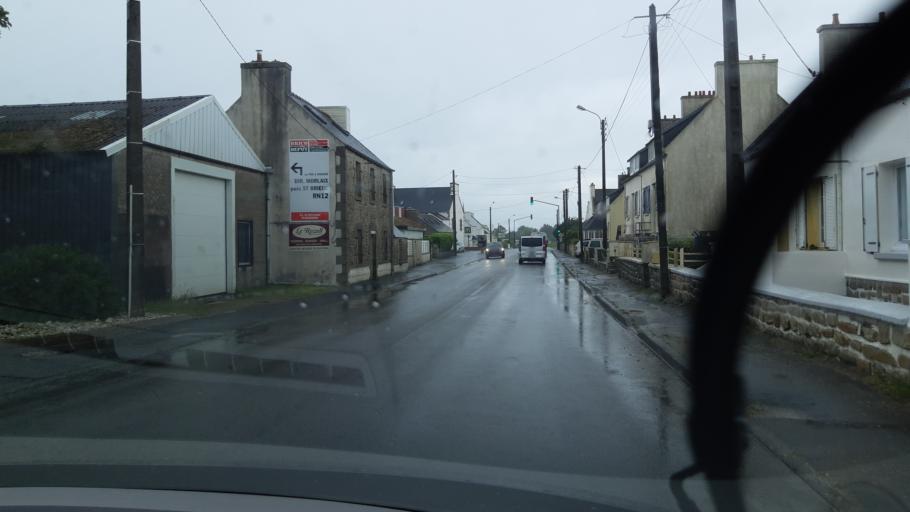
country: FR
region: Brittany
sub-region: Departement du Finistere
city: Plouvorn
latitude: 48.5792
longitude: -4.0480
